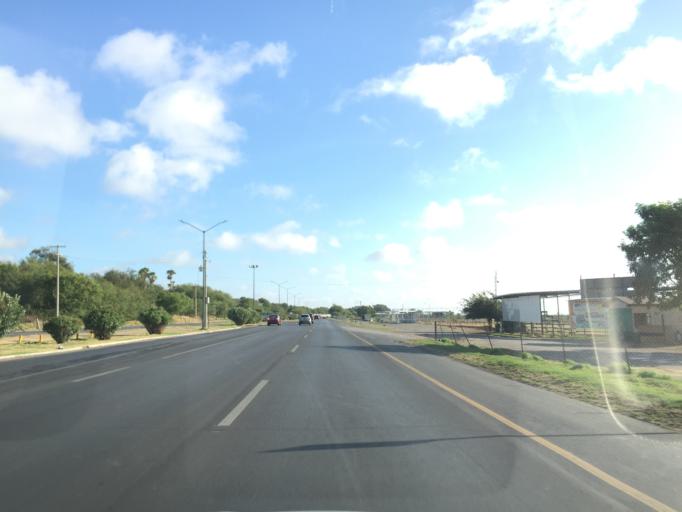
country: MX
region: Tamaulipas
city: Nuevo Laredo
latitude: 27.4674
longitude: -99.4866
